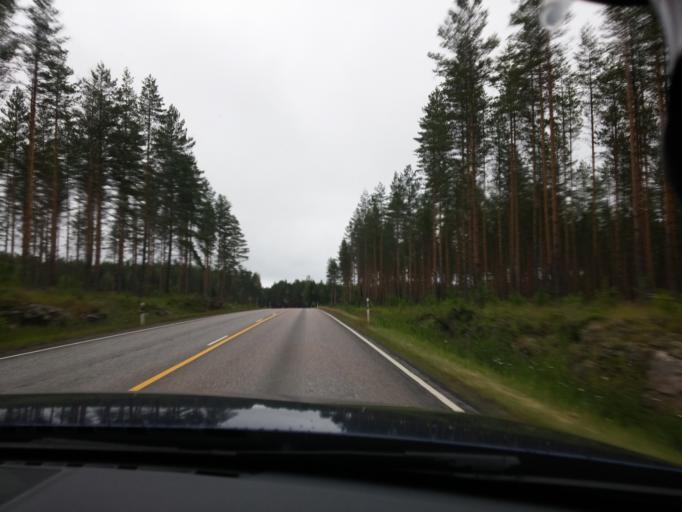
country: FI
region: Pirkanmaa
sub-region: Ylae-Pirkanmaa
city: Vilppula
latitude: 61.9210
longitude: 24.5378
